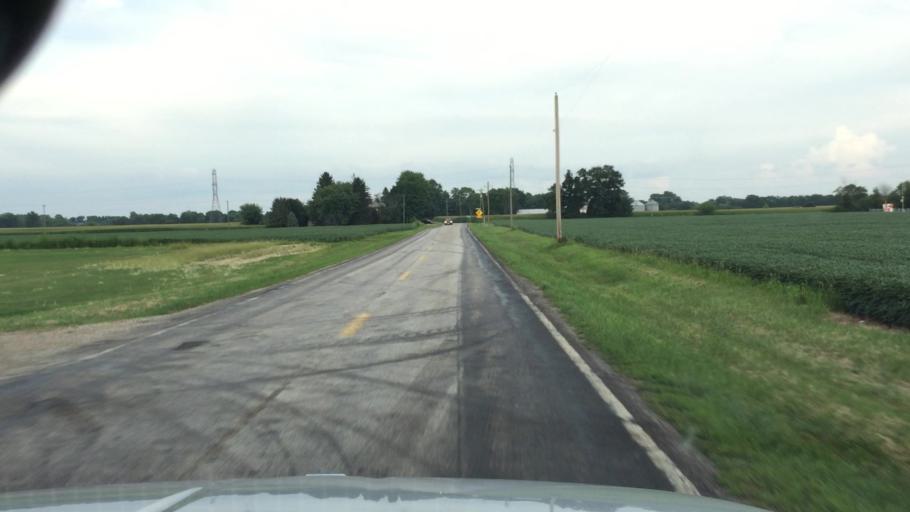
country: US
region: Ohio
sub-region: Franklin County
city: Hilliard
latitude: 40.0750
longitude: -83.2016
